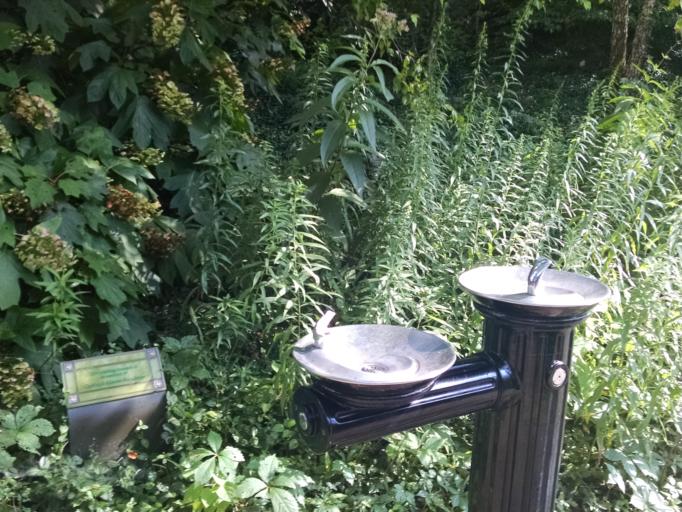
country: US
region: Missouri
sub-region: Saint Louis County
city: University City
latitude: 38.6354
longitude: -90.2871
